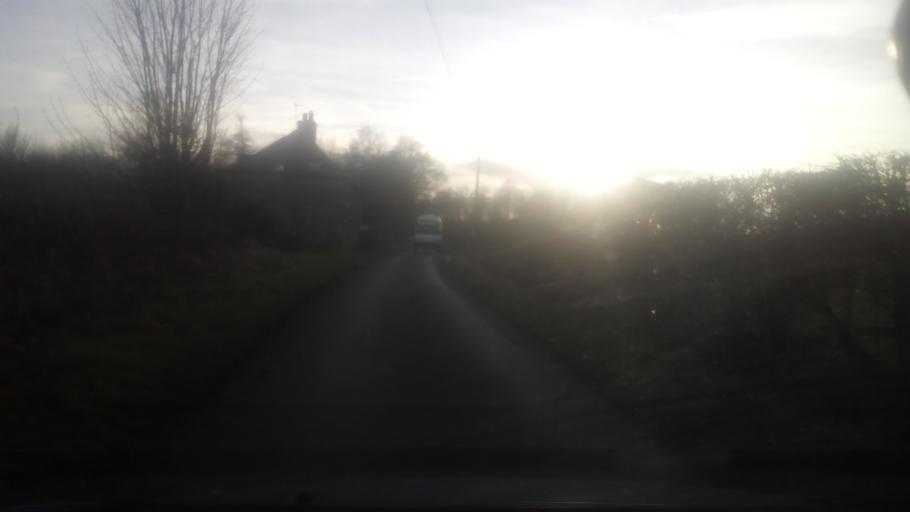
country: GB
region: Scotland
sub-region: The Scottish Borders
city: Jedburgh
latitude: 55.5006
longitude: -2.5514
